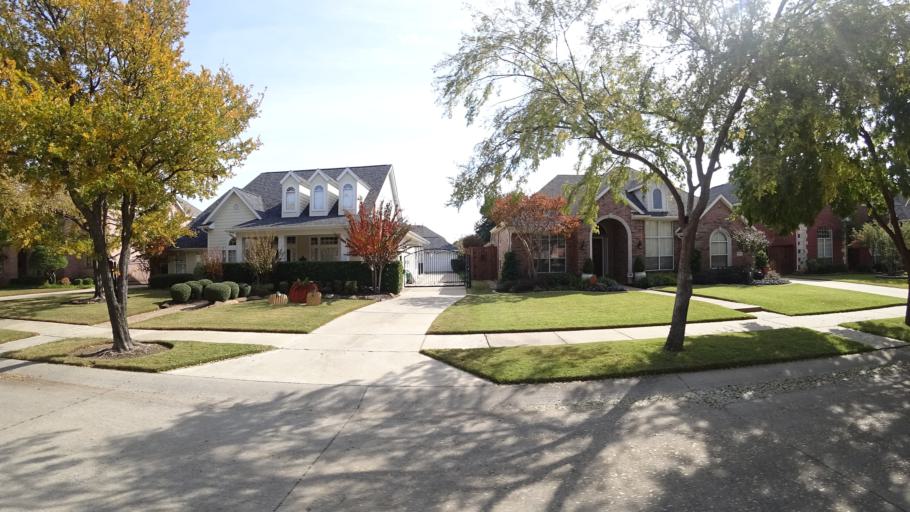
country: US
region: Texas
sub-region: Denton County
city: The Colony
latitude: 33.0304
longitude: -96.8949
